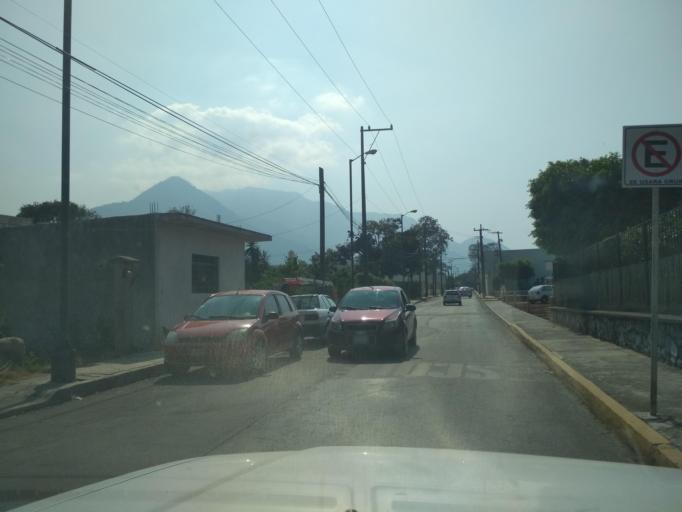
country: MX
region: Veracruz
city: Jalapilla
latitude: 18.8392
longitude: -97.0828
